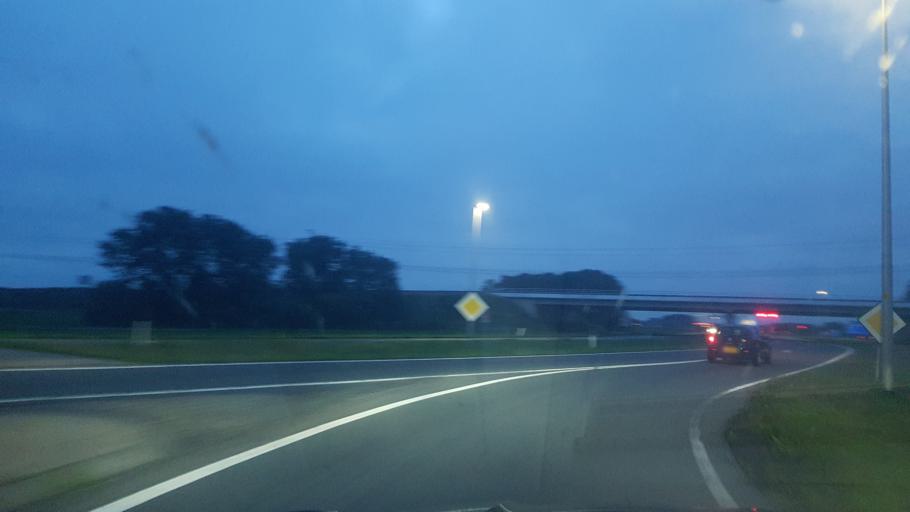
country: NL
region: Friesland
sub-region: Gemeente Boarnsterhim
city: Wergea
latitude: 53.1656
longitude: 5.8312
